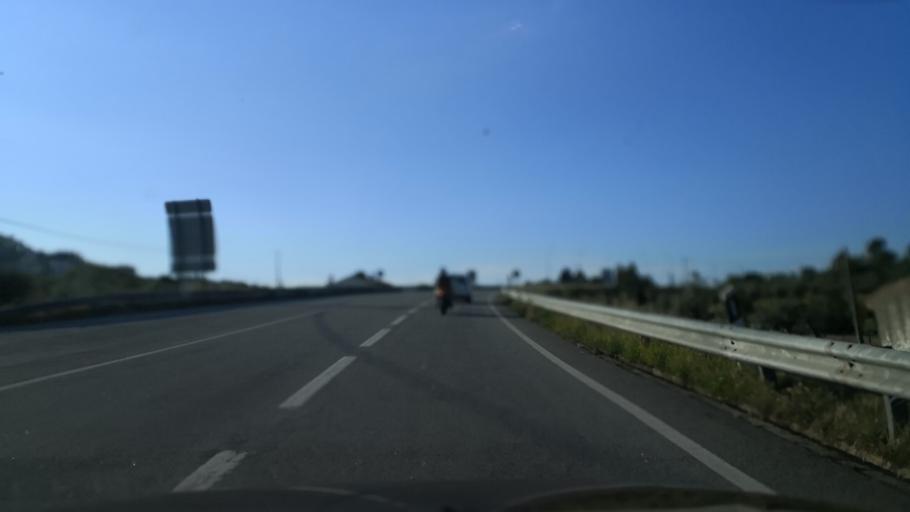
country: PT
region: Portalegre
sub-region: Portalegre
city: Portalegre
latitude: 39.3080
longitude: -7.4427
